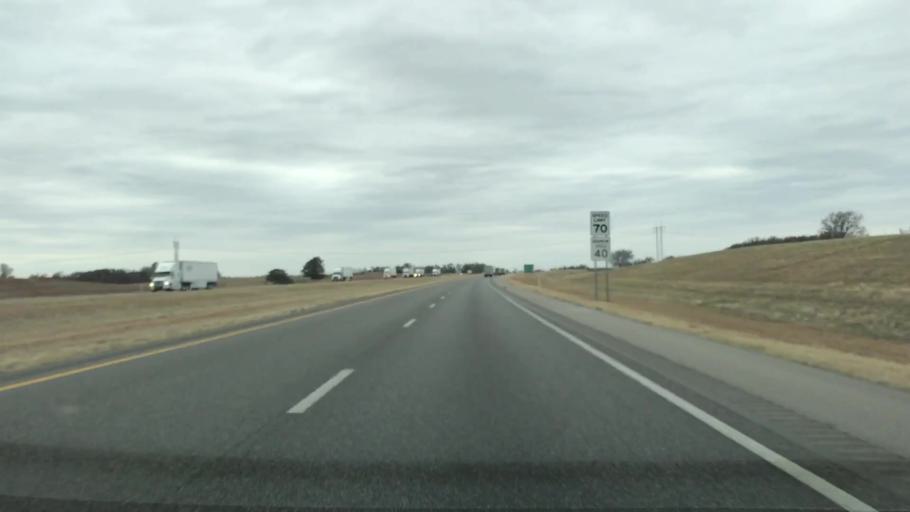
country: US
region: Oklahoma
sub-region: Beckham County
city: Erick
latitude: 35.2274
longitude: -99.9236
